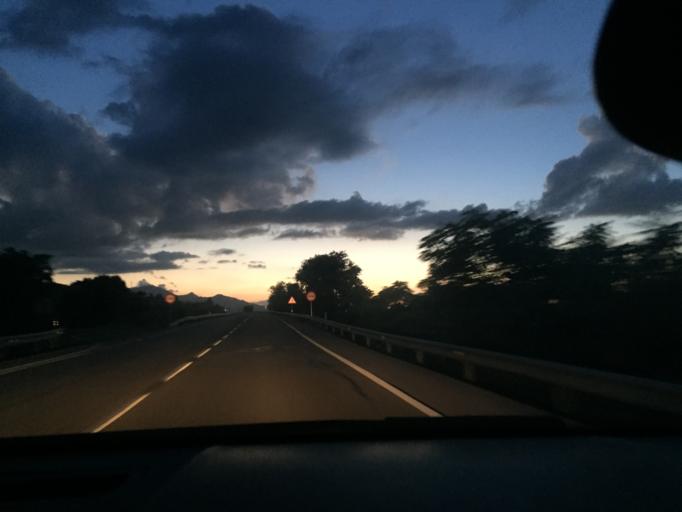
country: ES
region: Andalusia
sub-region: Provincia de Jaen
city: La Guardia de Jaen
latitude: 37.8044
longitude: -3.6791
